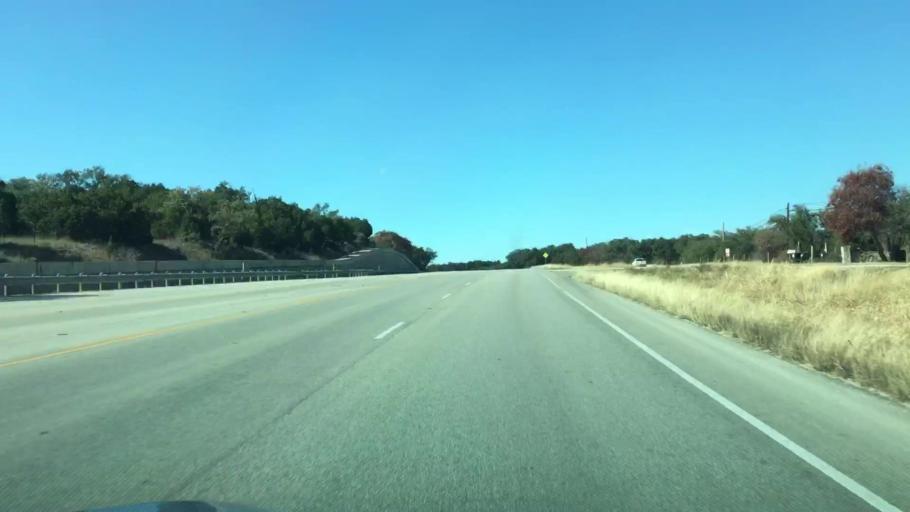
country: US
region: Texas
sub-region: Hays County
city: Dripping Springs
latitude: 30.2059
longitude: -98.1362
